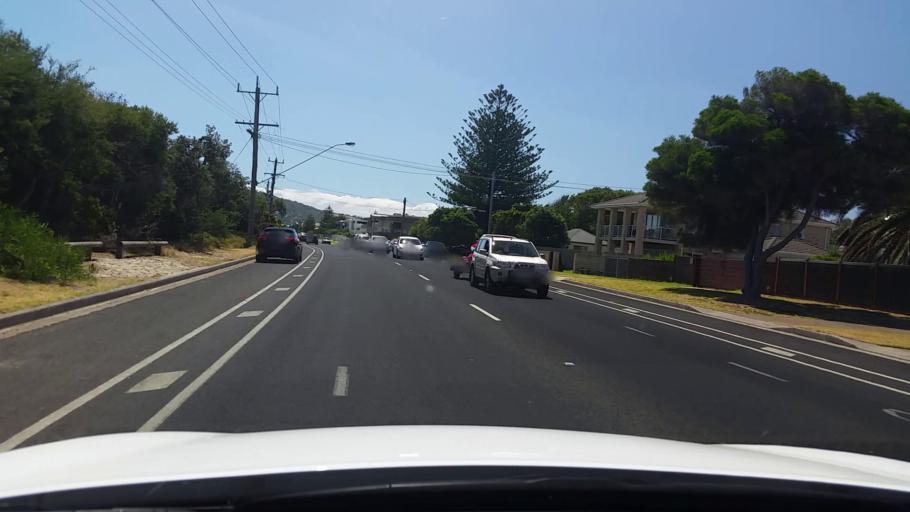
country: AU
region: Victoria
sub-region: Mornington Peninsula
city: Safety Beach
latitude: -38.3211
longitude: 144.9847
